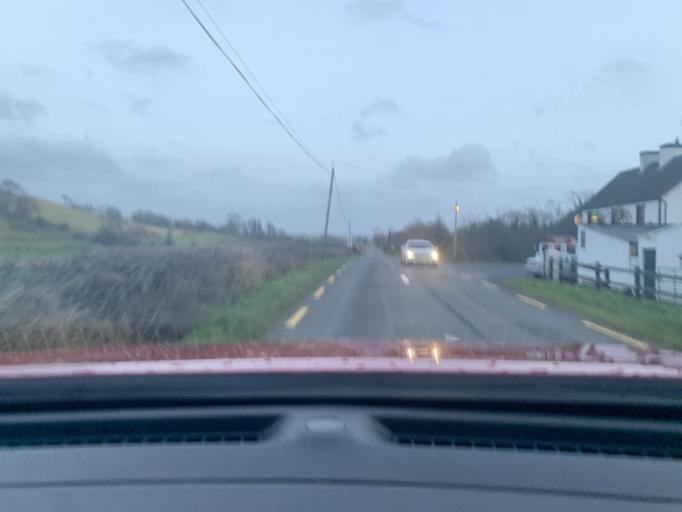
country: IE
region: Connaught
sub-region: Sligo
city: Ballymote
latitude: 54.0445
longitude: -8.4440
